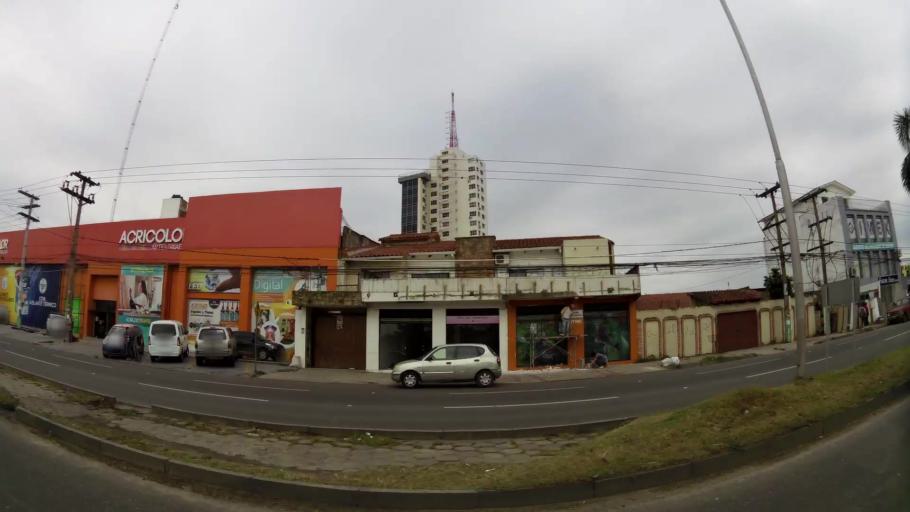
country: BO
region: Santa Cruz
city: Santa Cruz de la Sierra
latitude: -17.7596
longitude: -63.1802
